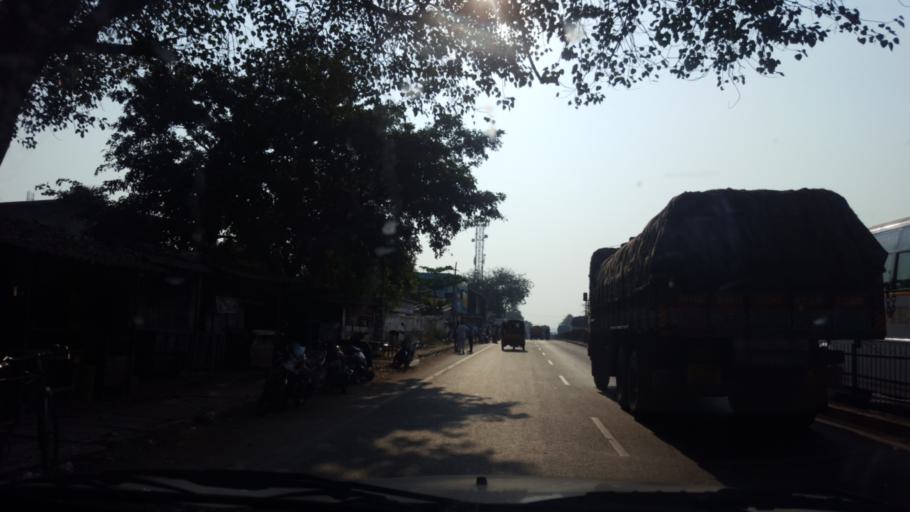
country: IN
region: Andhra Pradesh
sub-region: Vishakhapatnam
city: Etikoppaka
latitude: 17.4087
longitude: 82.7150
